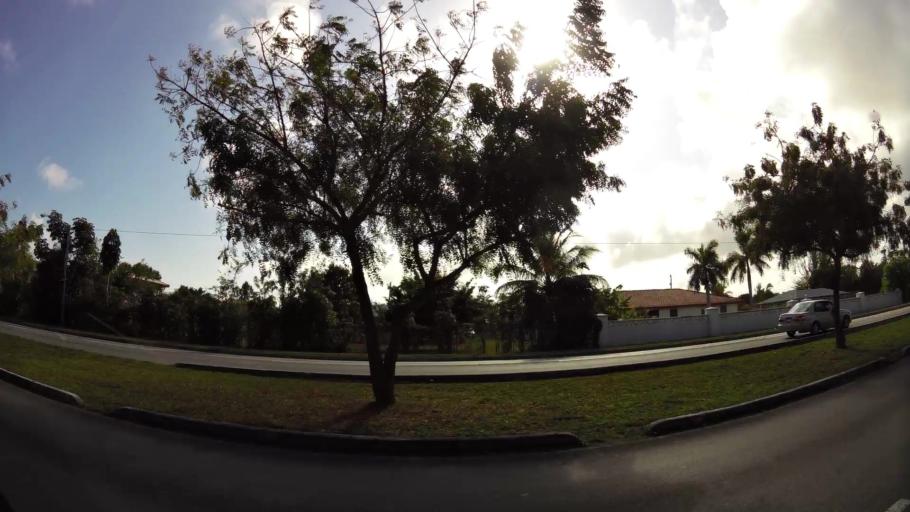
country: BS
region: Freeport
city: Lucaya
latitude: 26.5257
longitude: -78.6732
